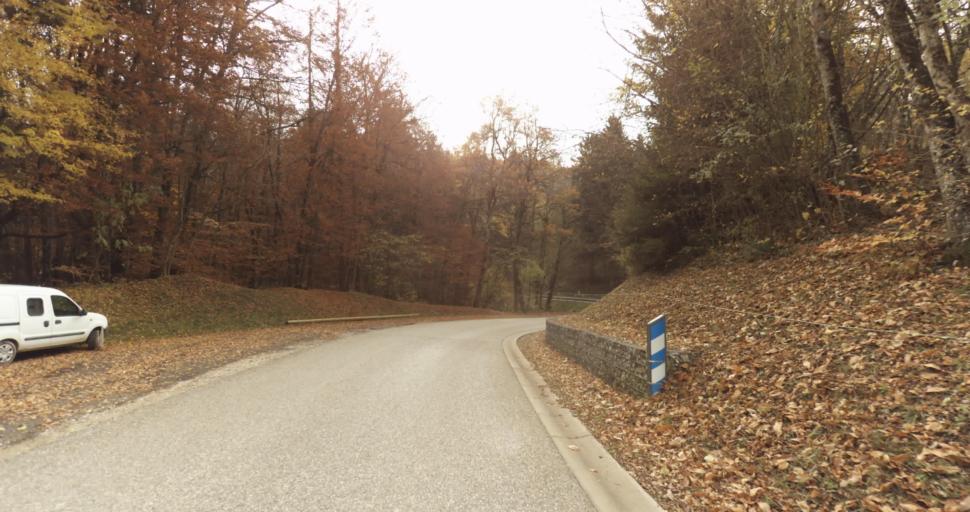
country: FR
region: Rhone-Alpes
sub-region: Departement de la Haute-Savoie
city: Epagny
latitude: 45.9628
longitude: 6.0942
